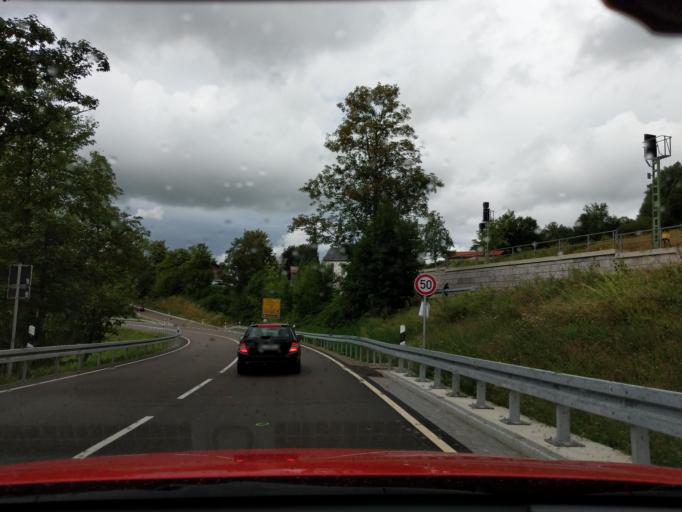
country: DE
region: Bavaria
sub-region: Swabia
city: Oberstaufen
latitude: 47.5511
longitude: 10.0267
